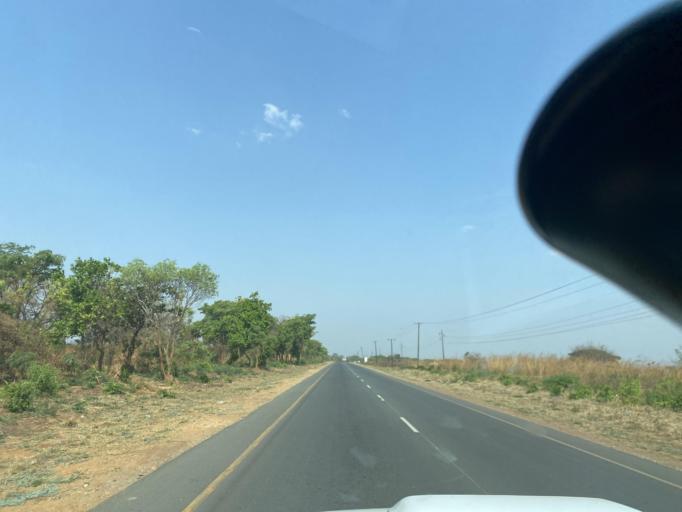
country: ZM
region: Lusaka
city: Lusaka
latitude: -15.3500
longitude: 28.1035
